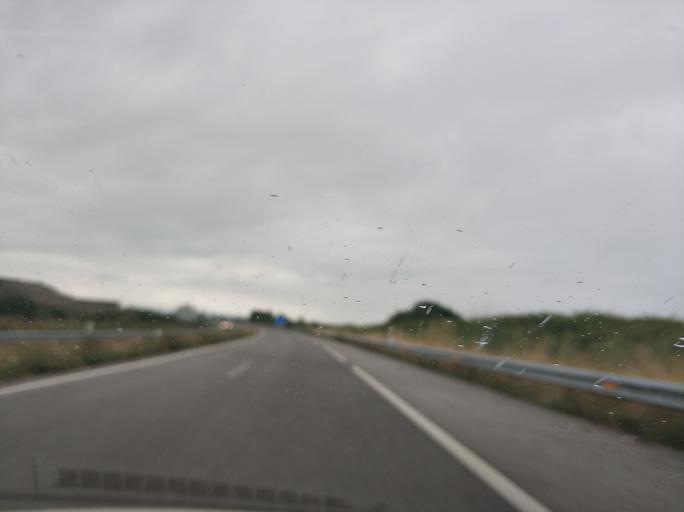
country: ES
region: Asturias
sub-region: Province of Asturias
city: Figueras
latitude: 43.5429
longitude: -6.9995
